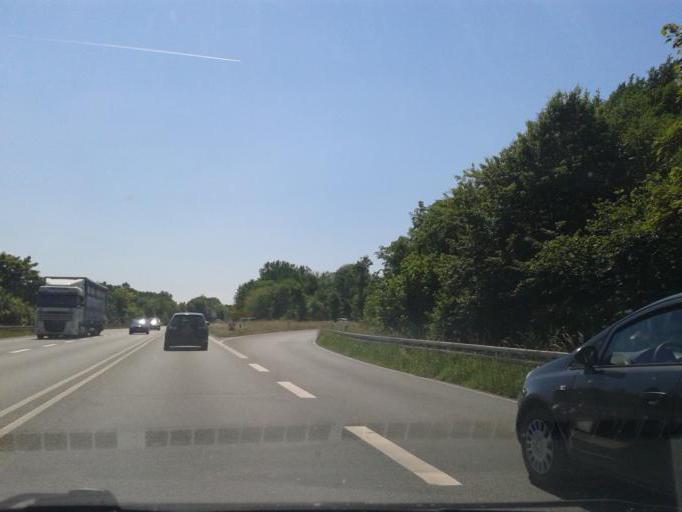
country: DE
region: North Rhine-Westphalia
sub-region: Regierungsbezirk Detmold
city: Paderborn
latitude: 51.7413
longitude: 8.7327
